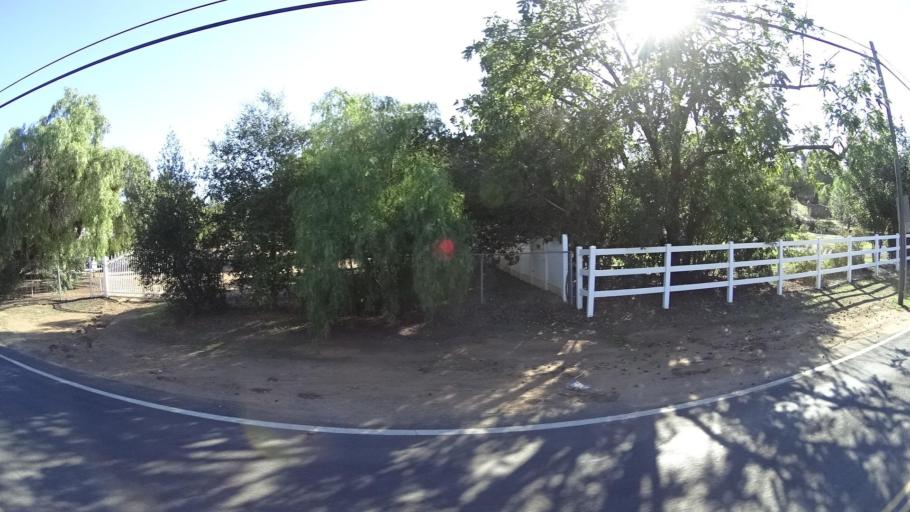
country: US
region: California
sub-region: San Diego County
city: Jamul
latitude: 32.7130
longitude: -116.8808
